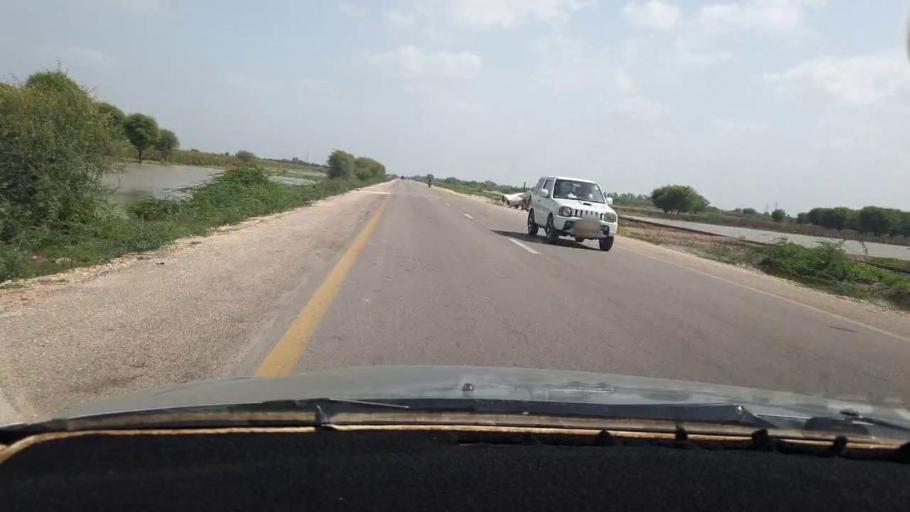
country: PK
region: Sindh
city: Digri
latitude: 25.1269
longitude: 69.1435
